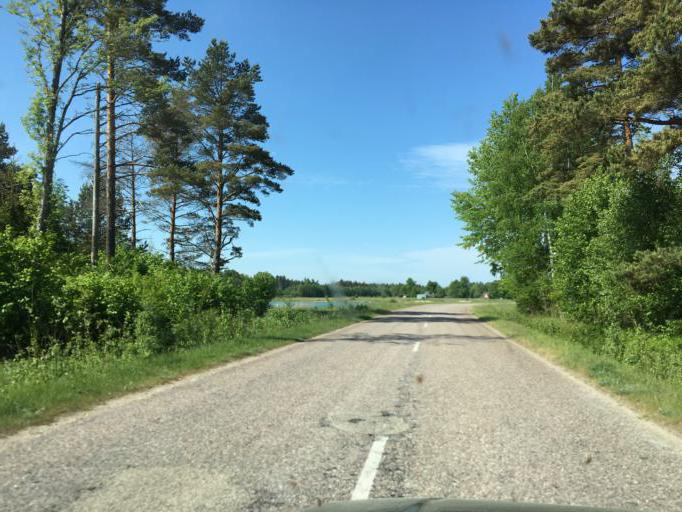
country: LV
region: Ventspils
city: Ventspils
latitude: 57.4830
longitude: 21.7706
